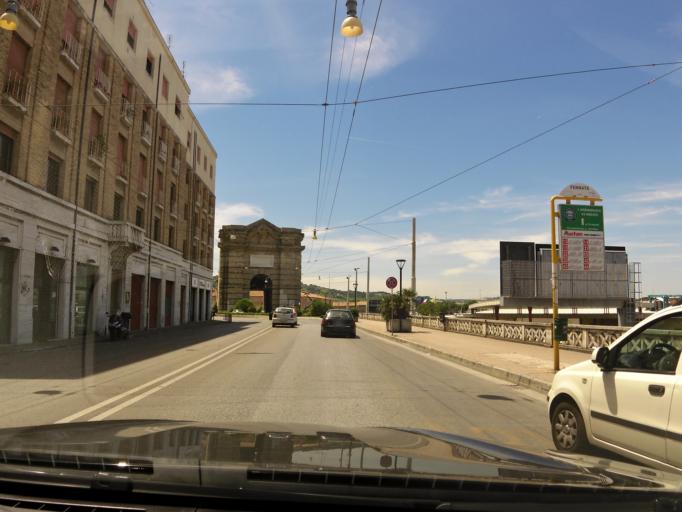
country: IT
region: The Marches
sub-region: Provincia di Ancona
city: Le Grazie di Ancona
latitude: 43.6161
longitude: 13.5062
